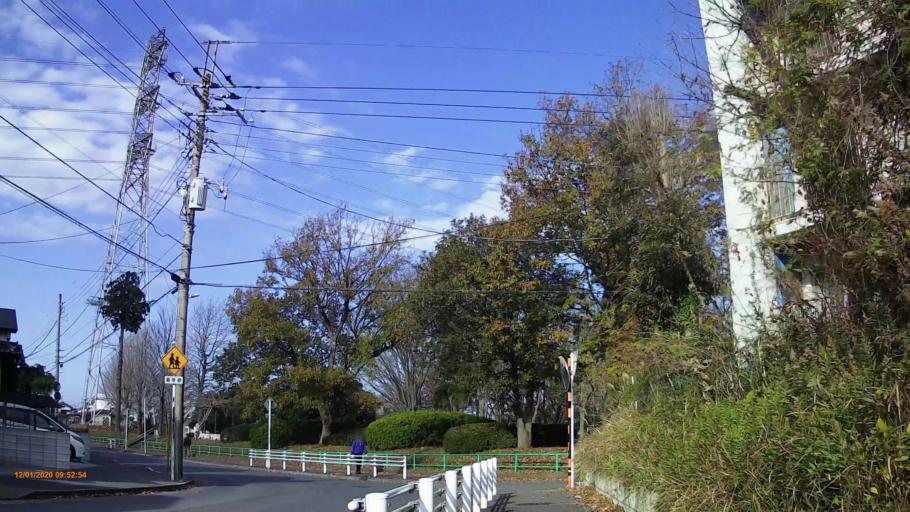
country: JP
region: Chiba
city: Yotsukaido
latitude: 35.6269
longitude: 140.1877
